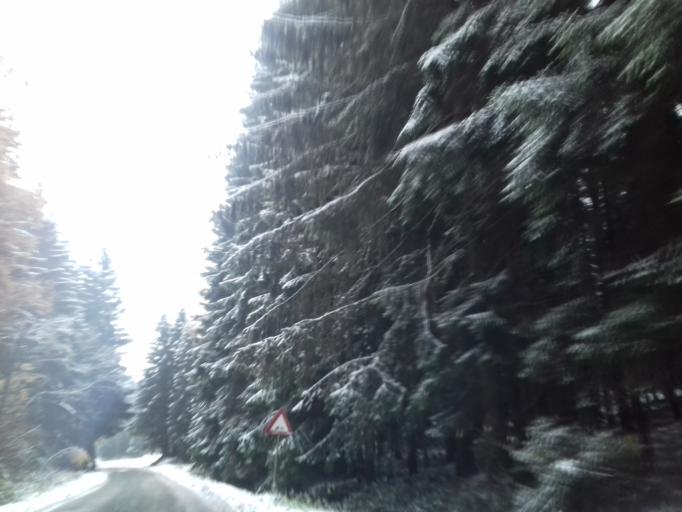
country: CZ
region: Plzensky
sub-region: Okres Domazlice
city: Klenci pod Cerchovem
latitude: 49.4376
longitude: 12.7911
